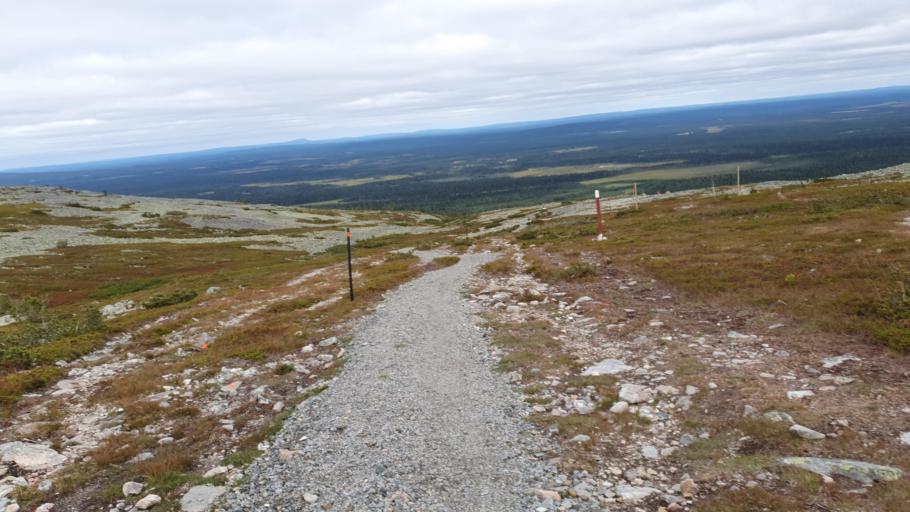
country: FI
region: Lapland
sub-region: Tunturi-Lappi
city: Kolari
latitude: 67.5684
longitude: 24.2402
